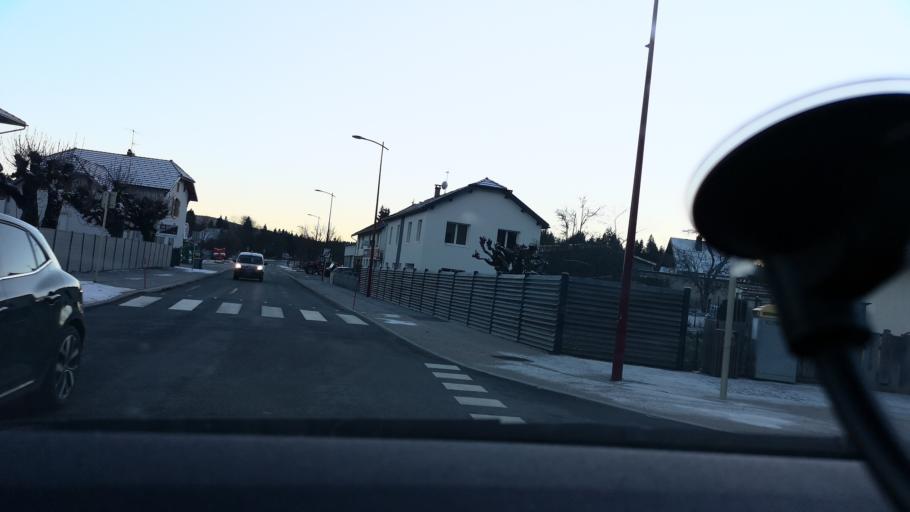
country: FR
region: Franche-Comte
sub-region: Departement du Doubs
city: Pontarlier
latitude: 46.8558
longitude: 6.3363
